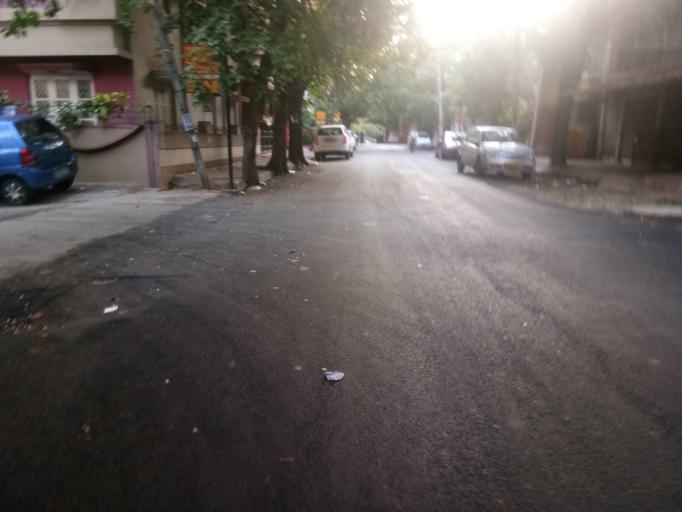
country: IN
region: Karnataka
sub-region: Bangalore Urban
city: Bangalore
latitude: 13.0181
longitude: 77.6357
